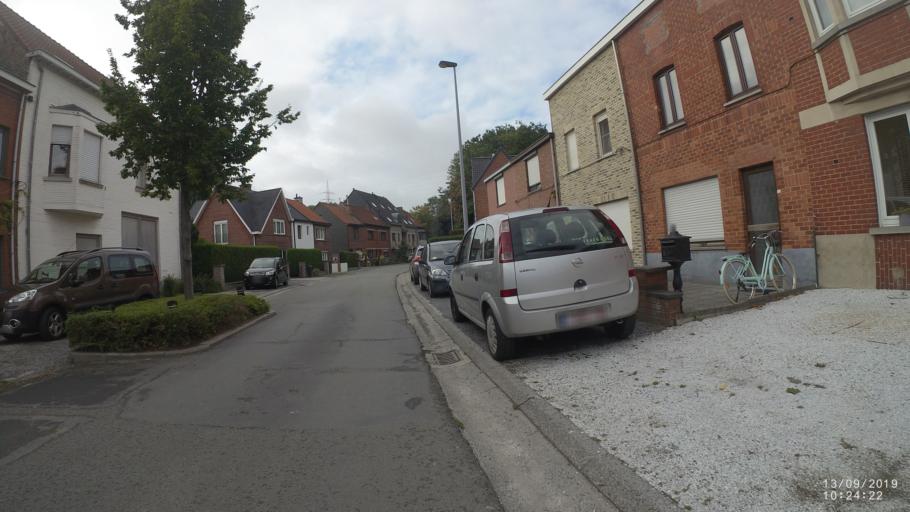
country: BE
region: Flanders
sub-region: Provincie Oost-Vlaanderen
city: Merelbeke
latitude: 51.0136
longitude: 3.7483
